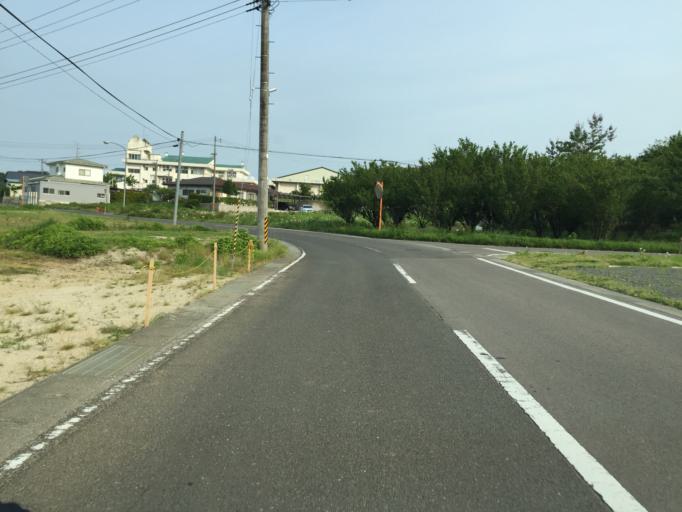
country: JP
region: Fukushima
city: Fukushima-shi
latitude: 37.7117
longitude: 140.4291
